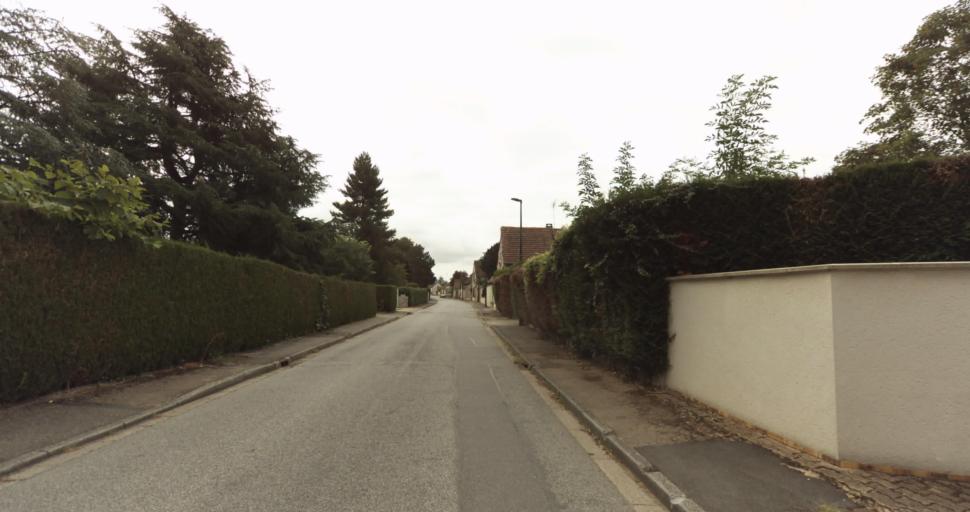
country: FR
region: Haute-Normandie
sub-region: Departement de l'Eure
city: Garennes-sur-Eure
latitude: 48.9141
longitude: 1.4346
